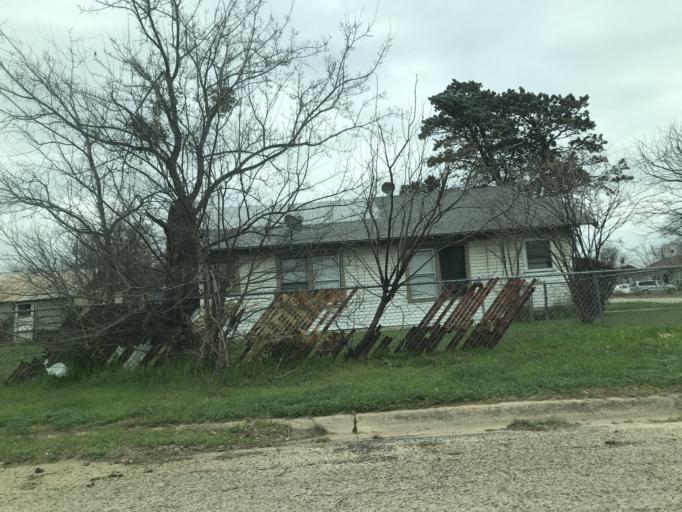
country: US
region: Texas
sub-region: Taylor County
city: Abilene
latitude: 32.4664
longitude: -99.7366
